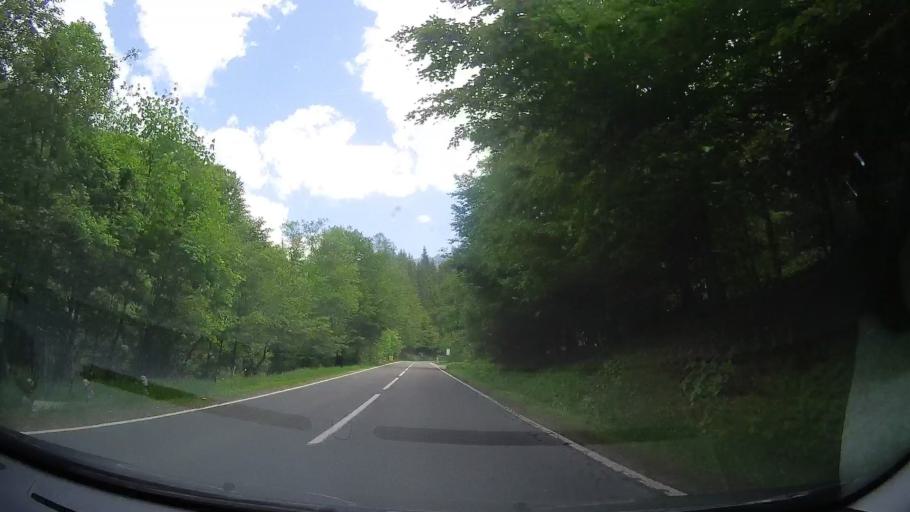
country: RO
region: Brasov
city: Crivina
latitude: 45.4565
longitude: 25.9500
